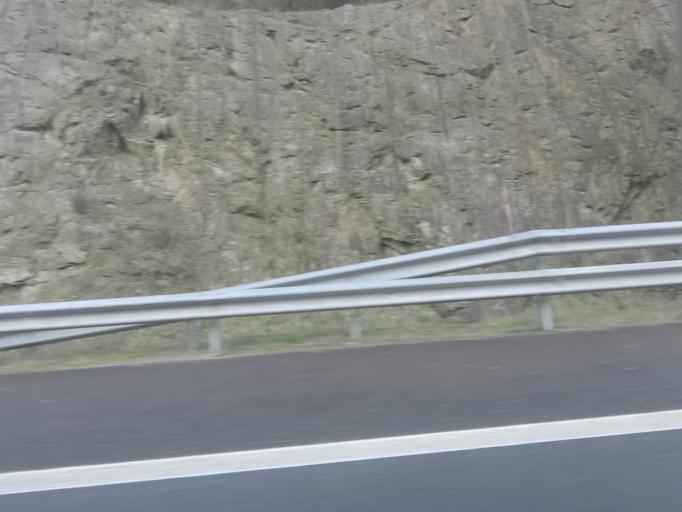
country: ES
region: Galicia
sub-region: Provincia da Coruna
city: Ribeira
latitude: 42.7408
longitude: -8.3709
